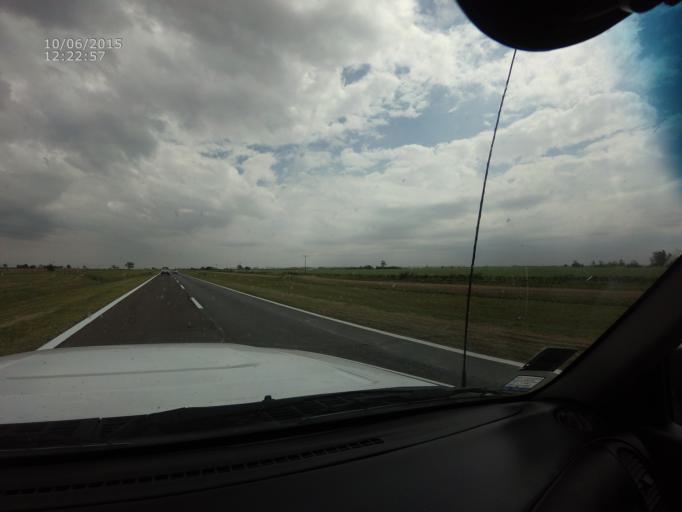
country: AR
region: Santa Fe
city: Roldan
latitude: -32.9160
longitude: -60.9470
